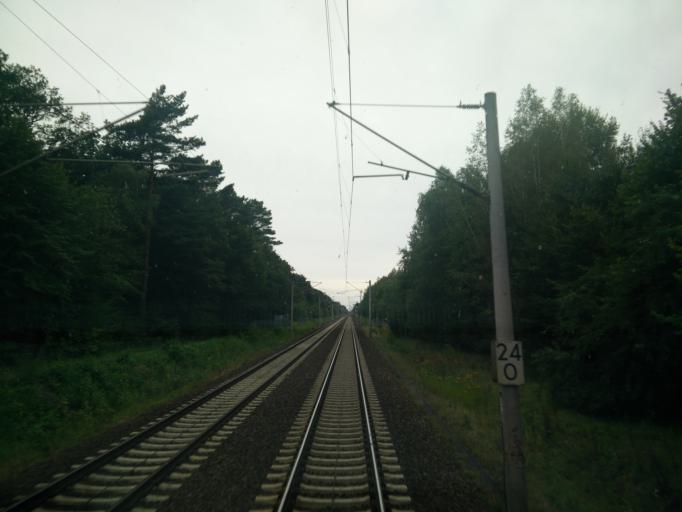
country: DE
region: Brandenburg
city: Dallgow-Doeberitz
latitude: 52.5724
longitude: 13.0406
